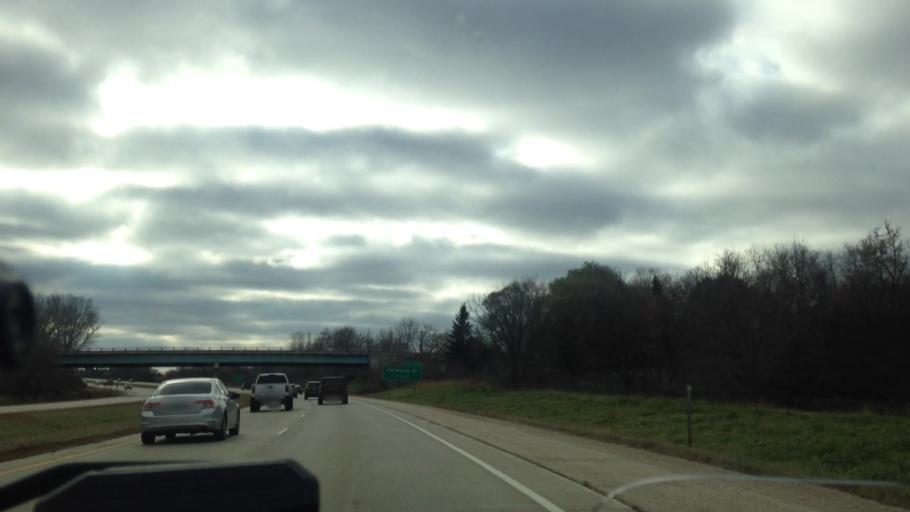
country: US
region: Wisconsin
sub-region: Washington County
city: West Bend
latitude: 43.4144
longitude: -88.2066
